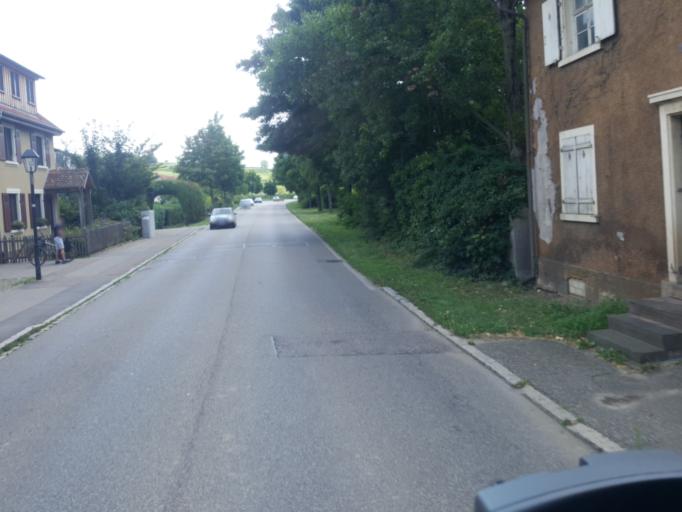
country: DE
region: Baden-Wuerttemberg
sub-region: Freiburg Region
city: Mullheim
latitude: 47.8289
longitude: 7.6208
